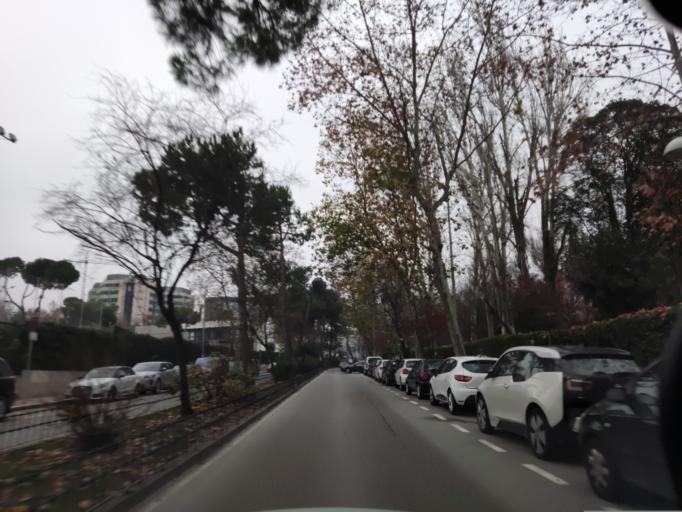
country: ES
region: Madrid
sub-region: Provincia de Madrid
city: Fuencarral-El Pardo
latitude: 40.4966
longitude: -3.7037
